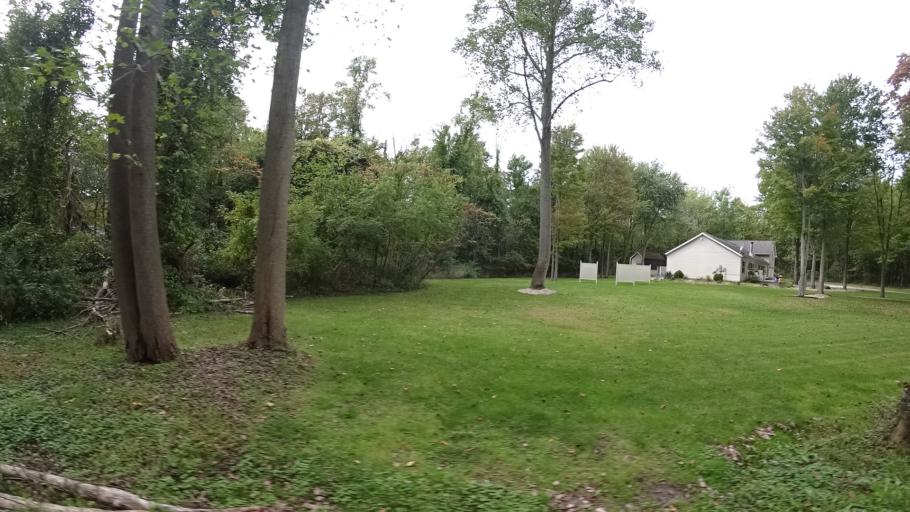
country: US
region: Indiana
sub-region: LaPorte County
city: Trail Creek
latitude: 41.6970
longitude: -86.8164
